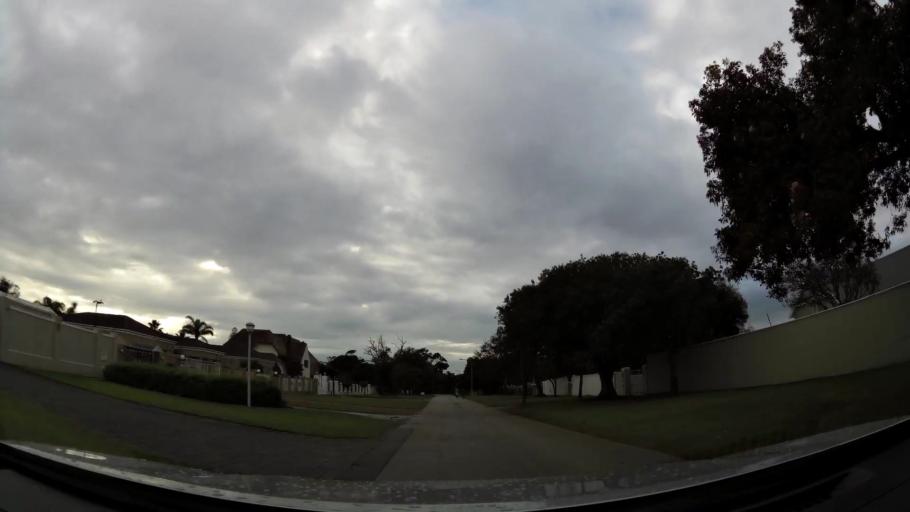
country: ZA
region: Eastern Cape
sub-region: Nelson Mandela Bay Metropolitan Municipality
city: Port Elizabeth
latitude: -33.9779
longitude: 25.5723
